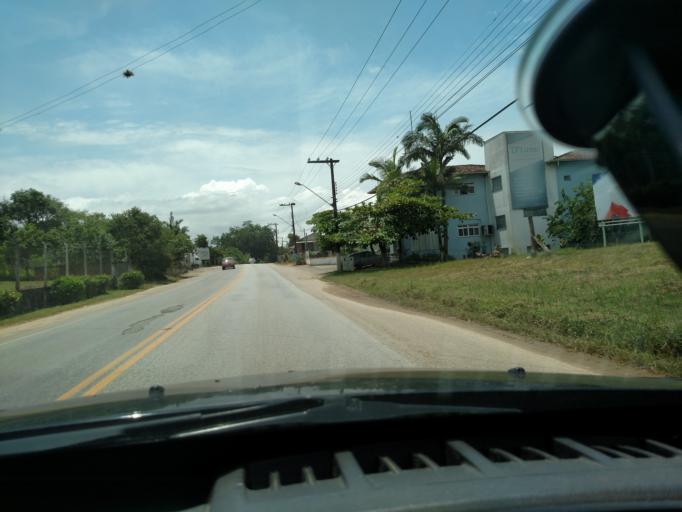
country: BR
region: Santa Catarina
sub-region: Gaspar
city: Gaspar
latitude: -26.9078
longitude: -48.8450
